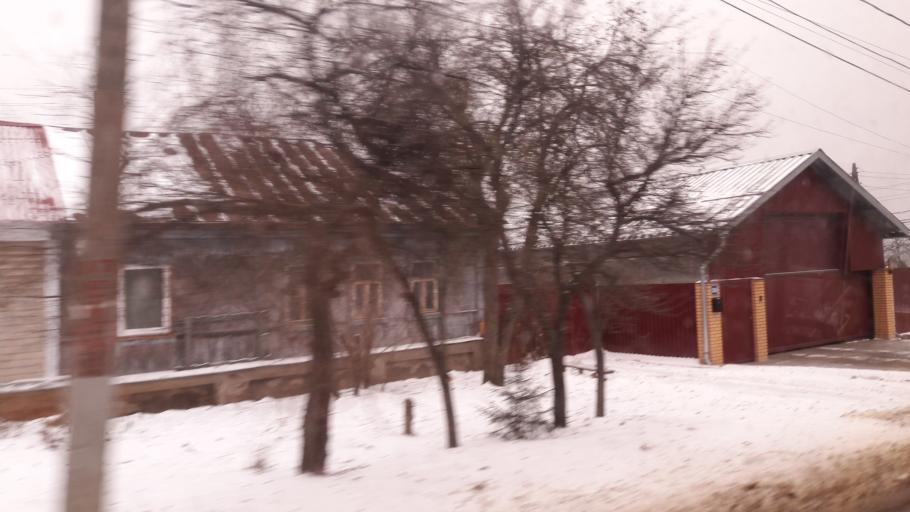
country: RU
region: Tula
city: Gorelki
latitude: 54.2346
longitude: 37.6316
